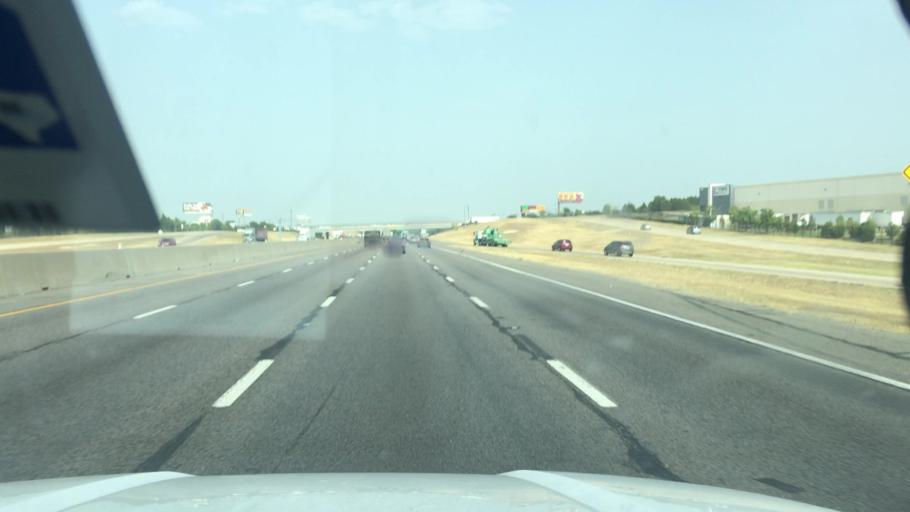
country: US
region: Texas
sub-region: Dallas County
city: DeSoto
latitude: 32.6437
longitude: -96.8460
